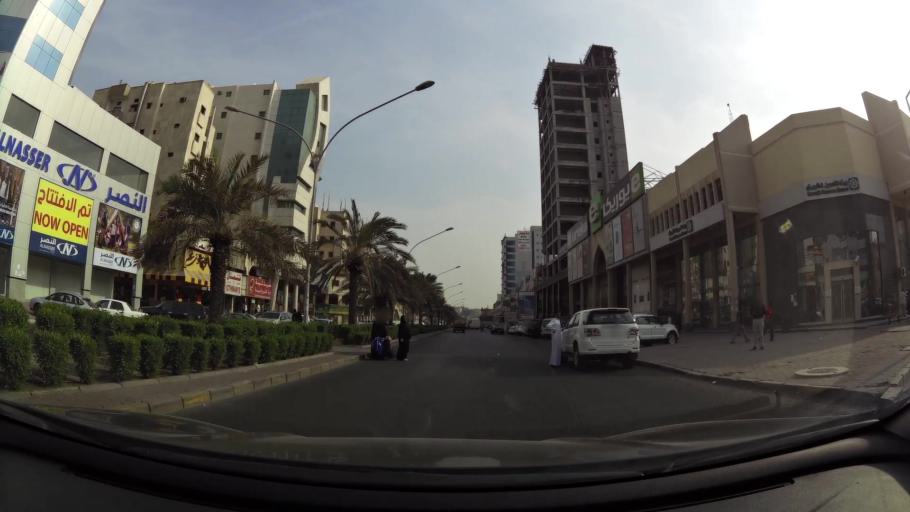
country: KW
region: Al Farwaniyah
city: Al Farwaniyah
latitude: 29.2785
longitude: 47.9619
